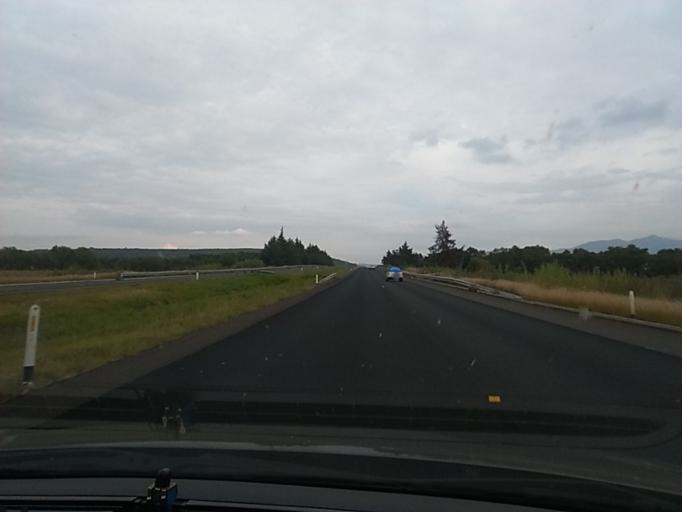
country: MX
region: Mexico
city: Huaniqueo de Morales
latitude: 19.9045
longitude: -101.5787
